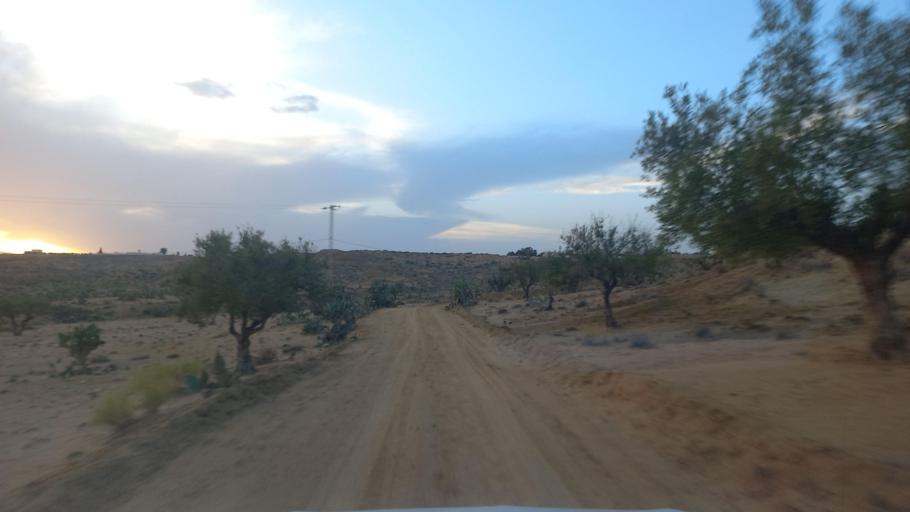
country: TN
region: Al Qasrayn
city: Kasserine
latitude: 35.2082
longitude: 9.0526
